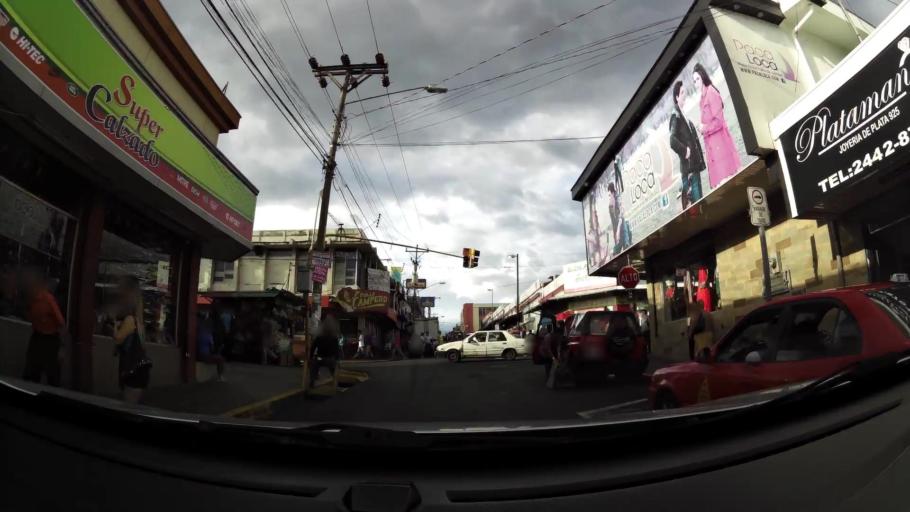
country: CR
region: Alajuela
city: Alajuela
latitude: 10.0154
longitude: -84.2158
